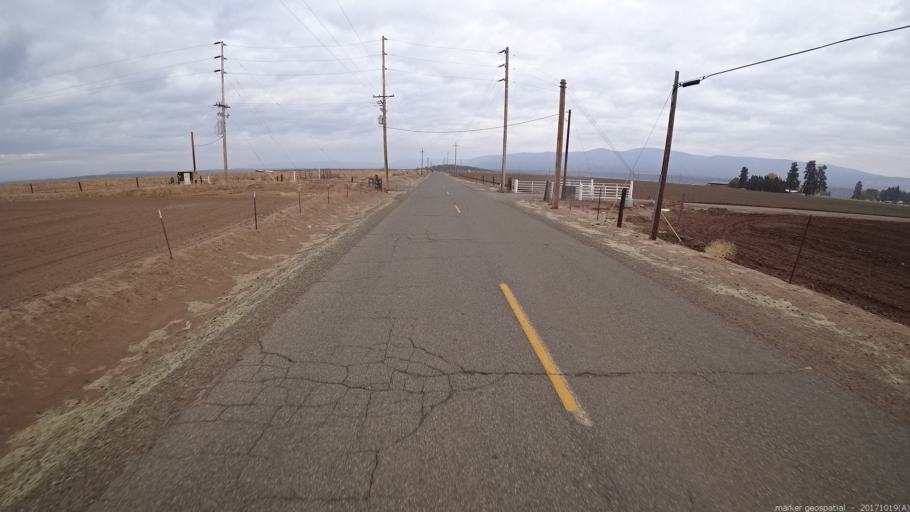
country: US
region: California
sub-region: Shasta County
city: Burney
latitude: 41.0729
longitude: -121.3652
